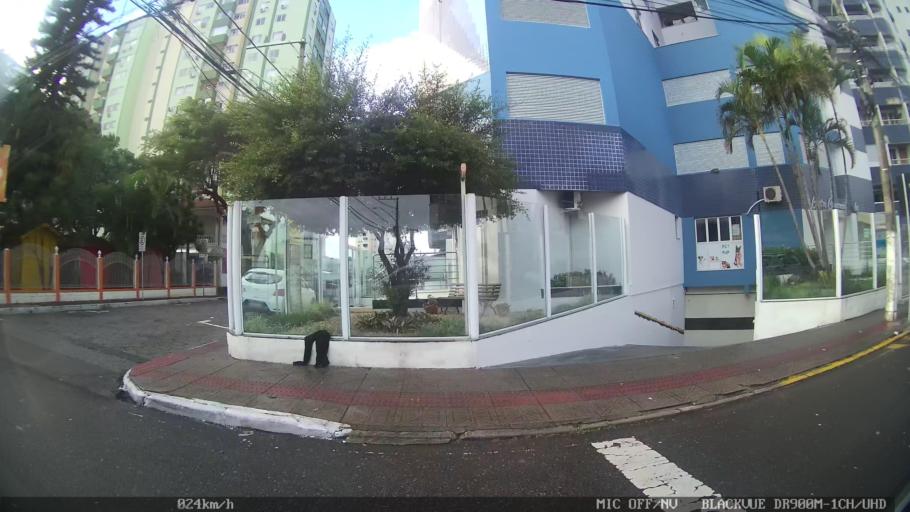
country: BR
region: Santa Catarina
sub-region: Sao Jose
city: Campinas
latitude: -27.5930
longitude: -48.6090
